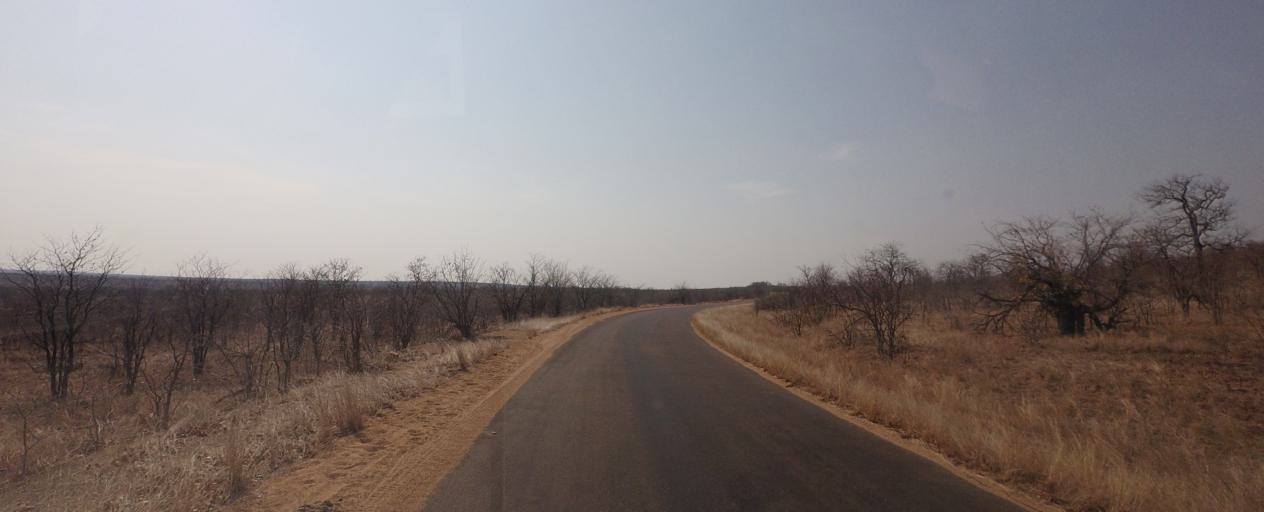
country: ZA
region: Limpopo
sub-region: Mopani District Municipality
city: Phalaborwa
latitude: -23.9703
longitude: 31.6290
